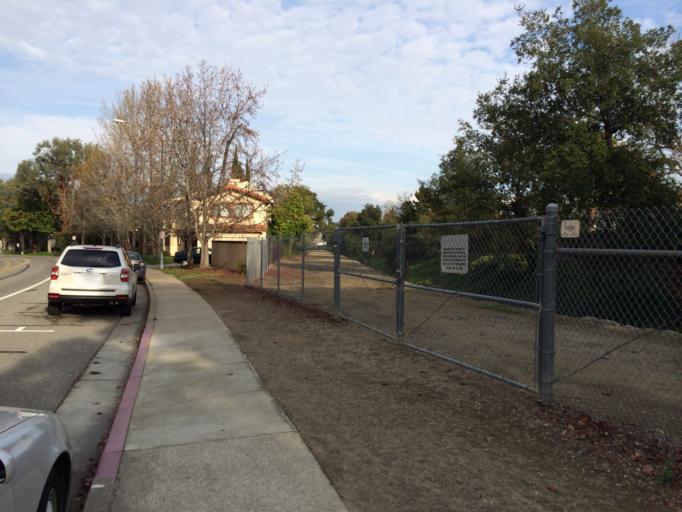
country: US
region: California
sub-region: Santa Clara County
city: Cupertino
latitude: 37.3193
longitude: -122.0276
